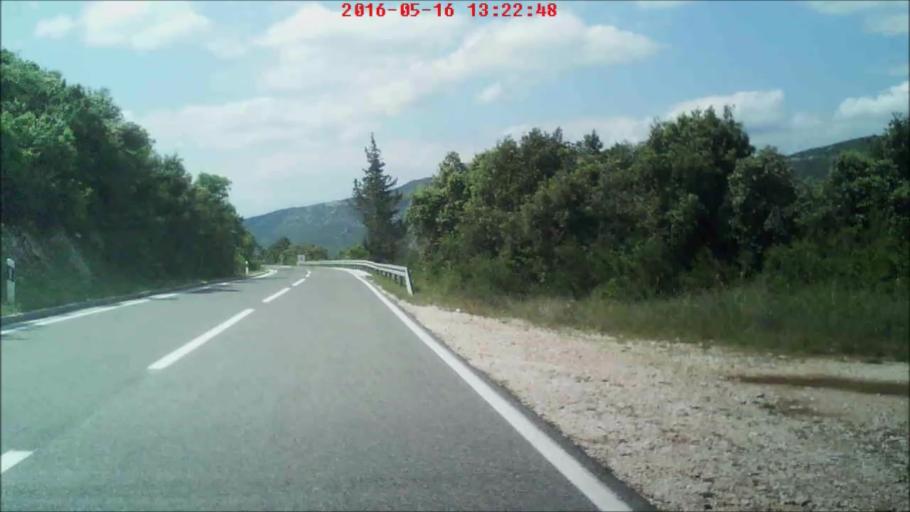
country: HR
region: Dubrovacko-Neretvanska
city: Ston
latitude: 42.8373
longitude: 17.7190
